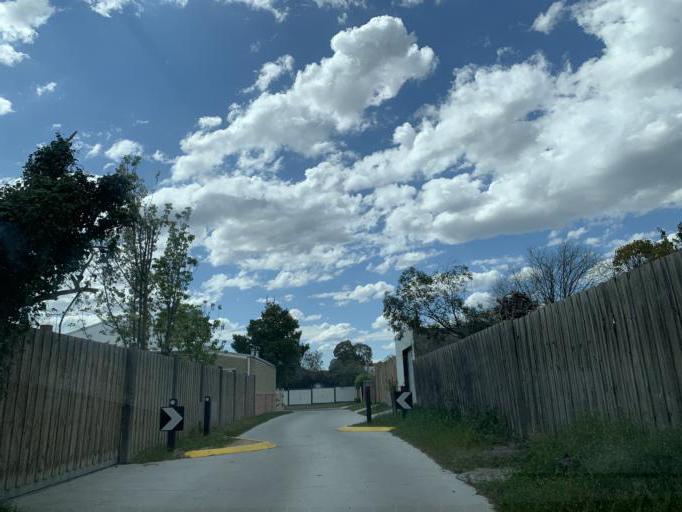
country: AU
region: Victoria
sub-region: Bayside
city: Cheltenham
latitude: -37.9628
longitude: 145.0445
